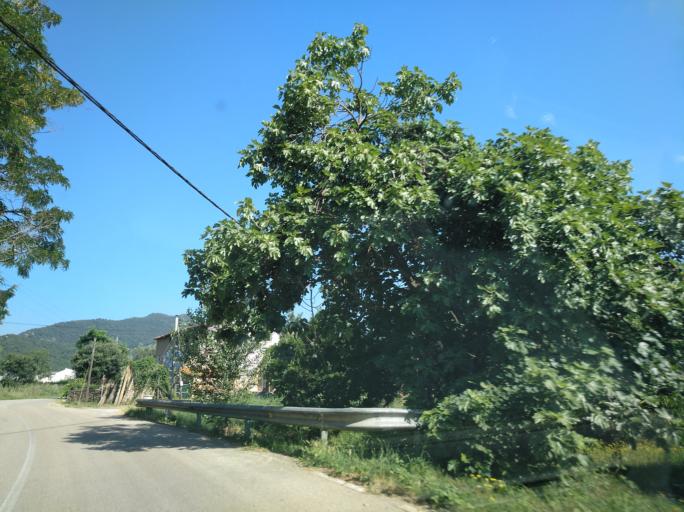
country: ES
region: Catalonia
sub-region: Provincia de Girona
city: la Cellera de Ter
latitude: 41.9751
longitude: 2.6187
